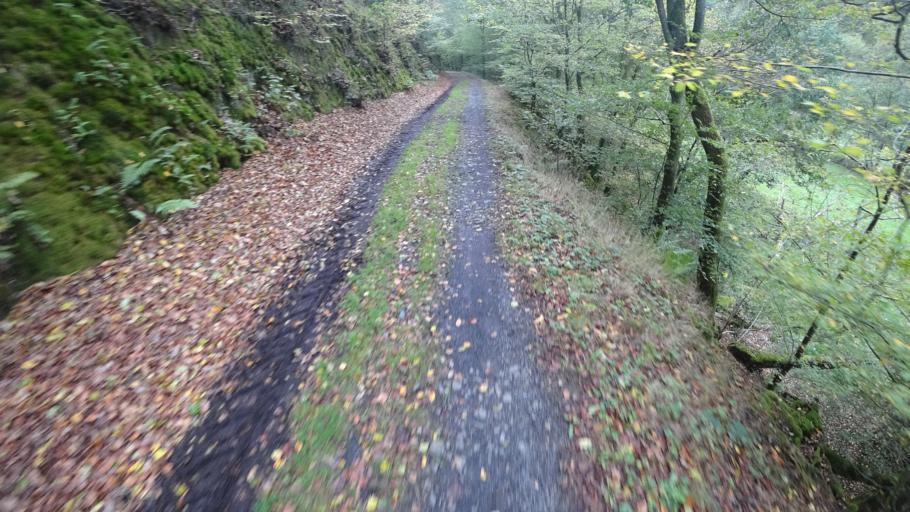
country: DE
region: Rheinland-Pfalz
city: Isselbach
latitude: 50.4052
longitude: 7.9049
